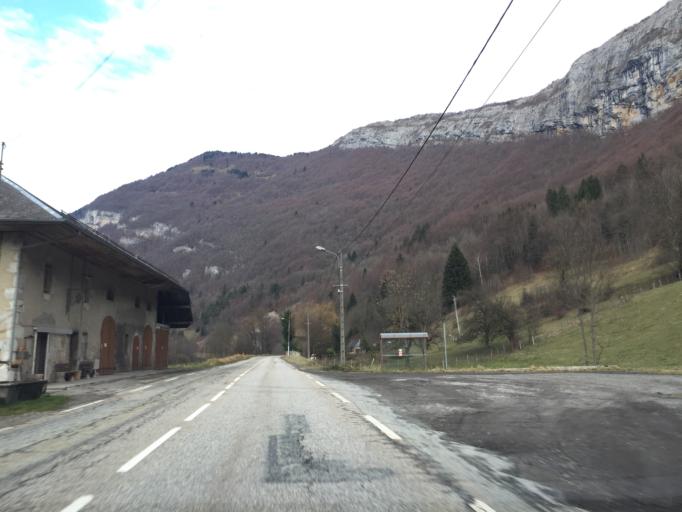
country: FR
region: Rhone-Alpes
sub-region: Departement de la Haute-Savoie
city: Gruffy
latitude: 45.7379
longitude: 6.0982
